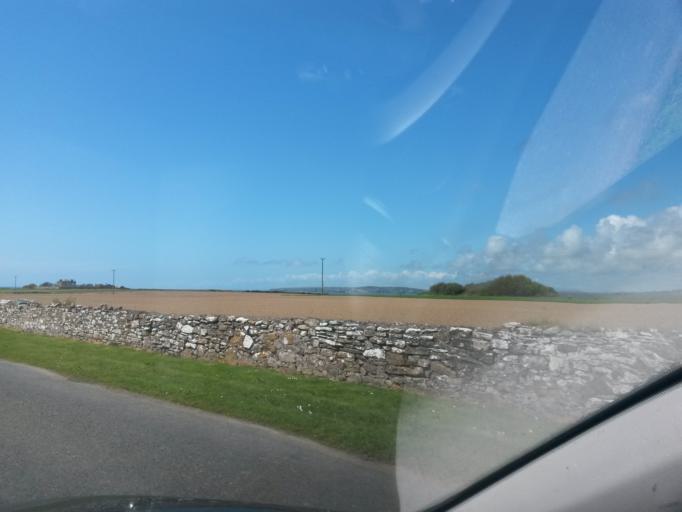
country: IE
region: Munster
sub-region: Waterford
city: Dunmore East
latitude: 52.1532
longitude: -6.8991
